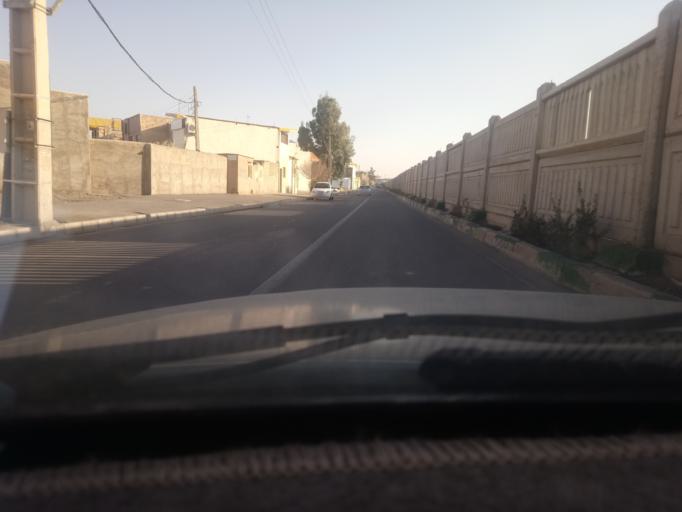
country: IR
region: Qom
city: Qom
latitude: 34.6654
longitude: 50.8672
